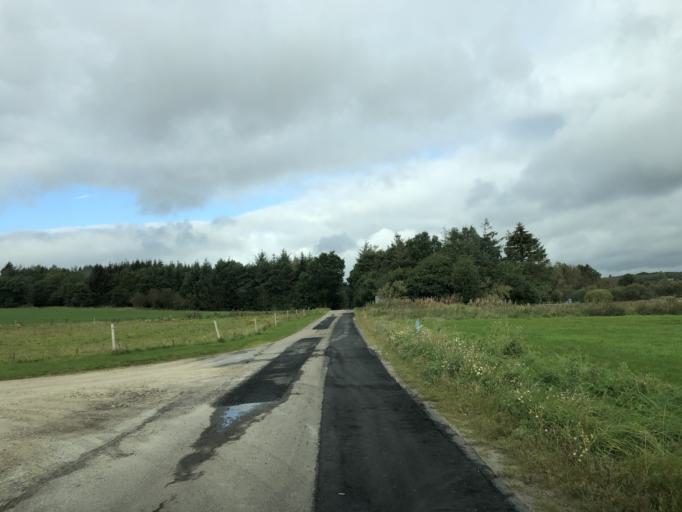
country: DK
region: Central Jutland
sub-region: Holstebro Kommune
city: Ulfborg
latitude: 56.3017
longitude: 8.4388
